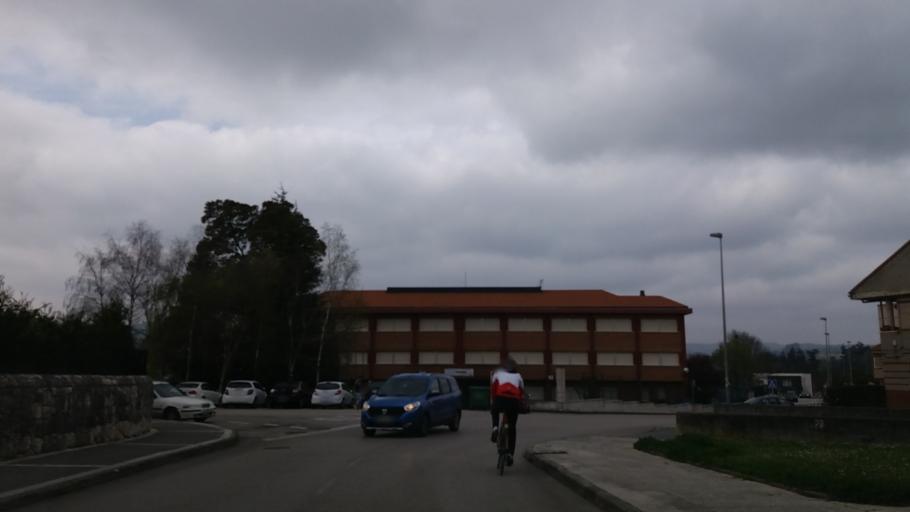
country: ES
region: Cantabria
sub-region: Provincia de Cantabria
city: Reocin
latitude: 43.3630
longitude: -4.0833
